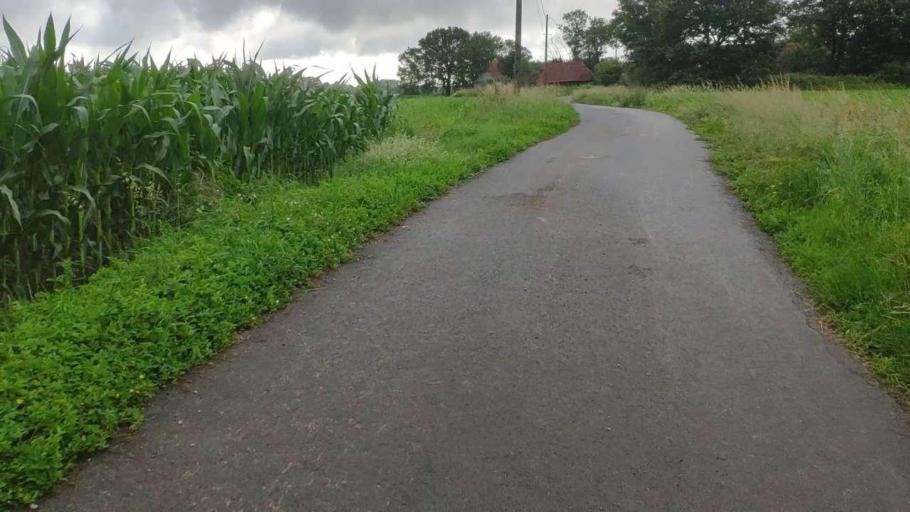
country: FR
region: Franche-Comte
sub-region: Departement du Jura
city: Bletterans
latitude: 46.8516
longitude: 5.4532
